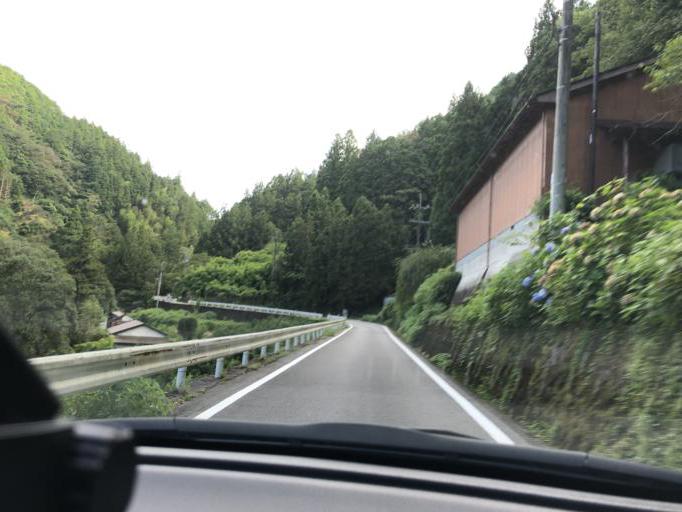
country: JP
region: Kochi
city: Kochi-shi
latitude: 33.6188
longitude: 133.4960
